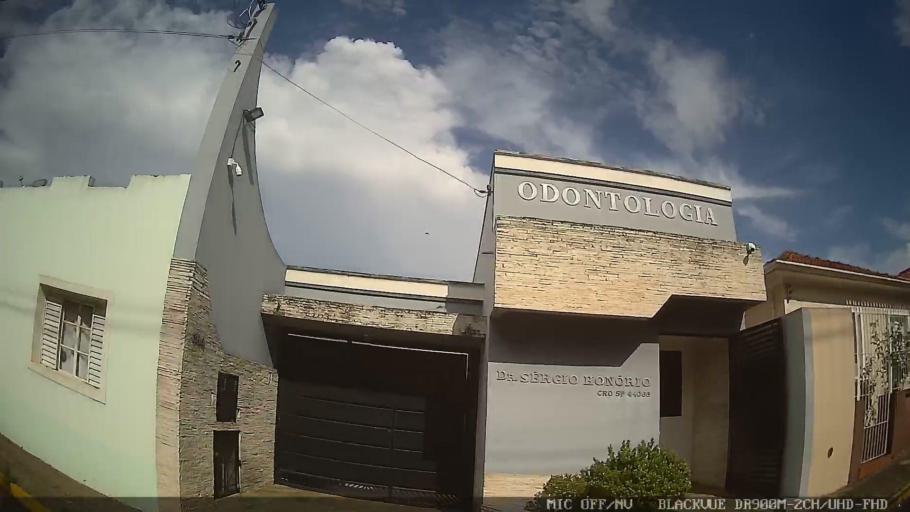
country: BR
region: Sao Paulo
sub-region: Laranjal Paulista
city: Laranjal Paulista
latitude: -23.0462
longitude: -47.8353
